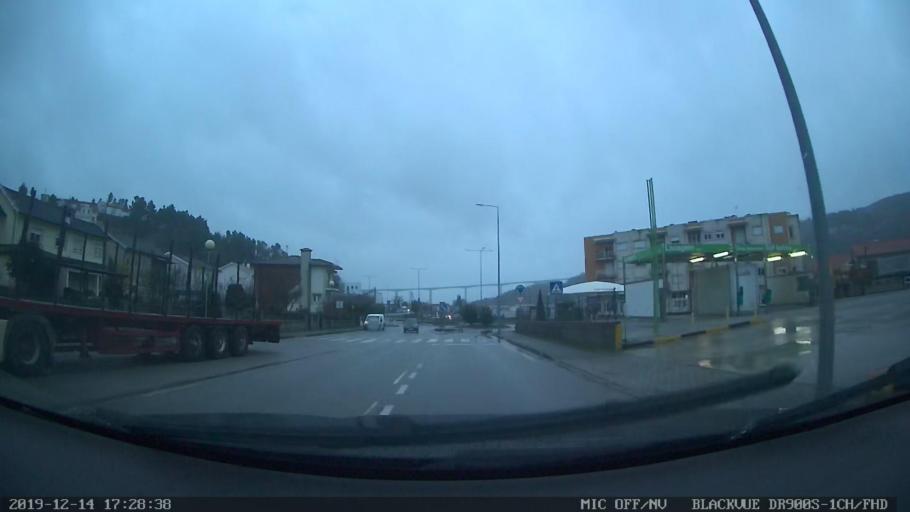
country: PT
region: Vila Real
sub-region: Vila Pouca de Aguiar
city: Vila Pouca de Aguiar
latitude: 41.4942
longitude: -7.6444
